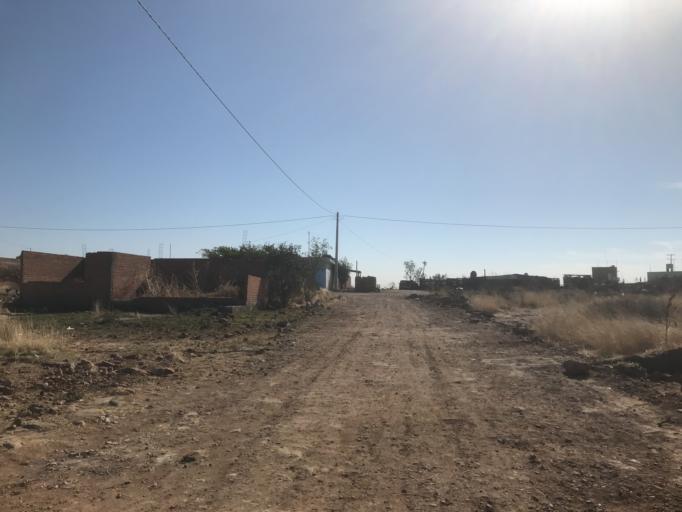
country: MX
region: Durango
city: Victoria de Durango
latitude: 24.0451
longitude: -104.7021
